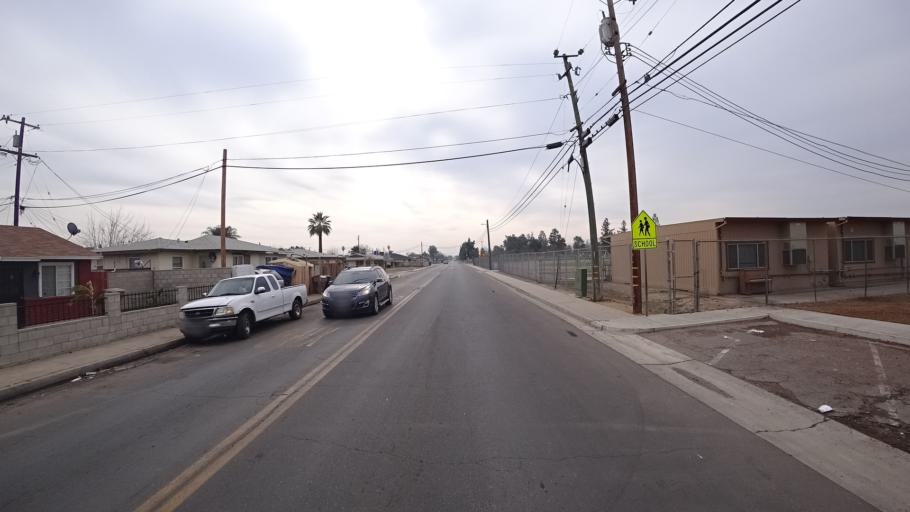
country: US
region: California
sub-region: Kern County
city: Bakersfield
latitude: 35.3663
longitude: -118.9909
